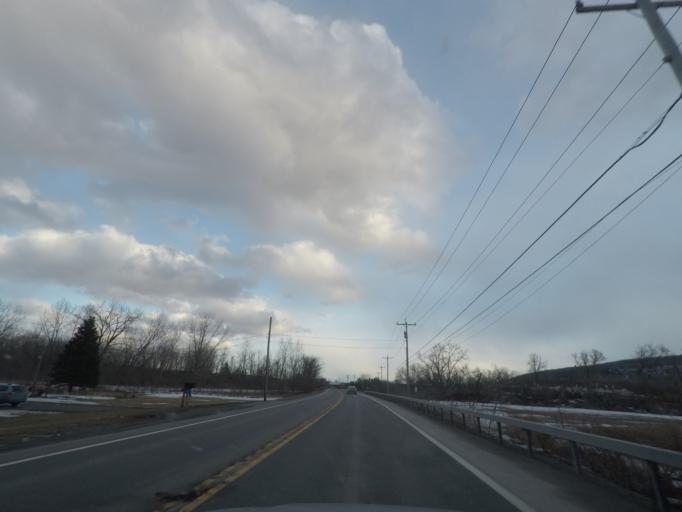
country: US
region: New York
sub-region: Herkimer County
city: Frankfort
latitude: 43.0778
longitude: -75.1142
